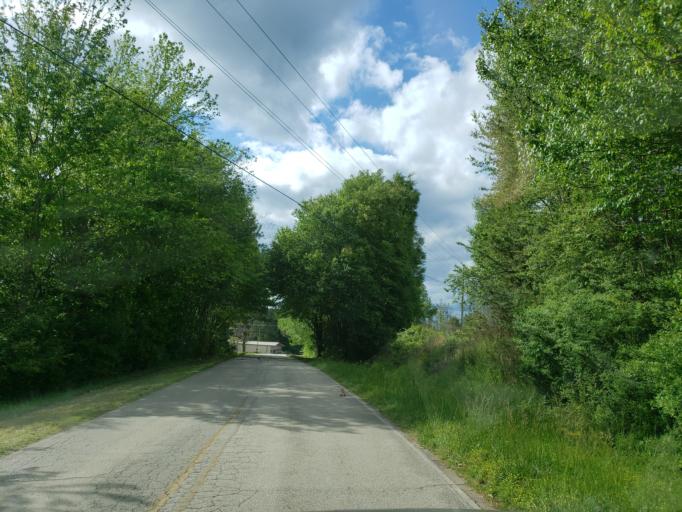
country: US
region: Georgia
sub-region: Haralson County
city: Tallapoosa
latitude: 33.6759
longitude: -85.2907
